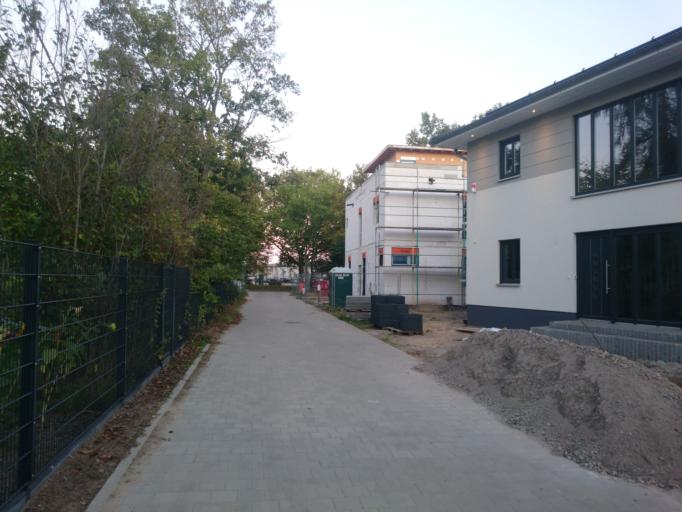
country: DE
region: Berlin
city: Tegel
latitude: 52.5667
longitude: 13.2982
